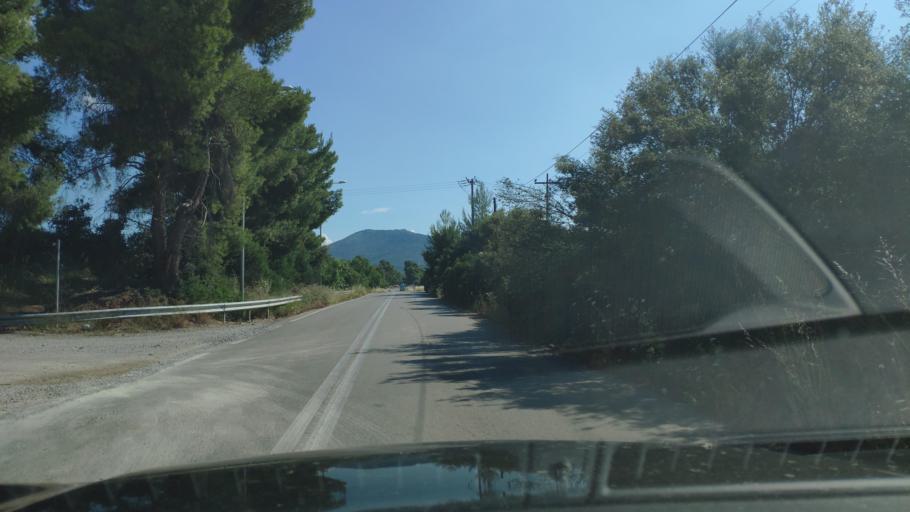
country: GR
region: Central Greece
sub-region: Nomos Voiotias
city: Arma
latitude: 38.3950
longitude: 23.5105
